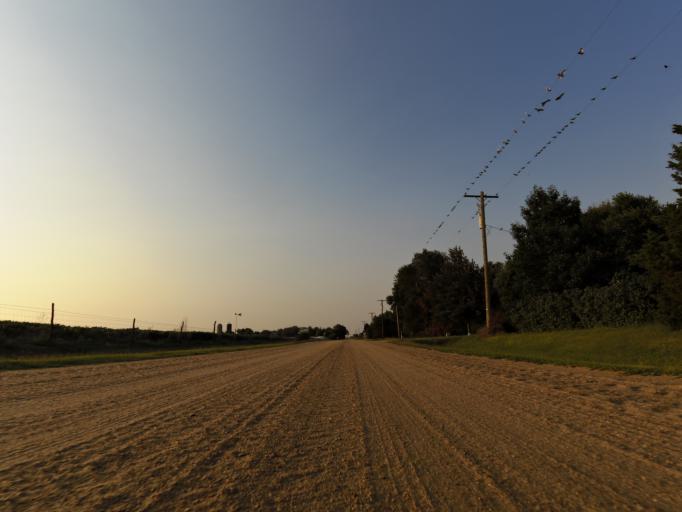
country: US
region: Kansas
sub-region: Reno County
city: South Hutchinson
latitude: 38.0093
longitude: -97.9954
